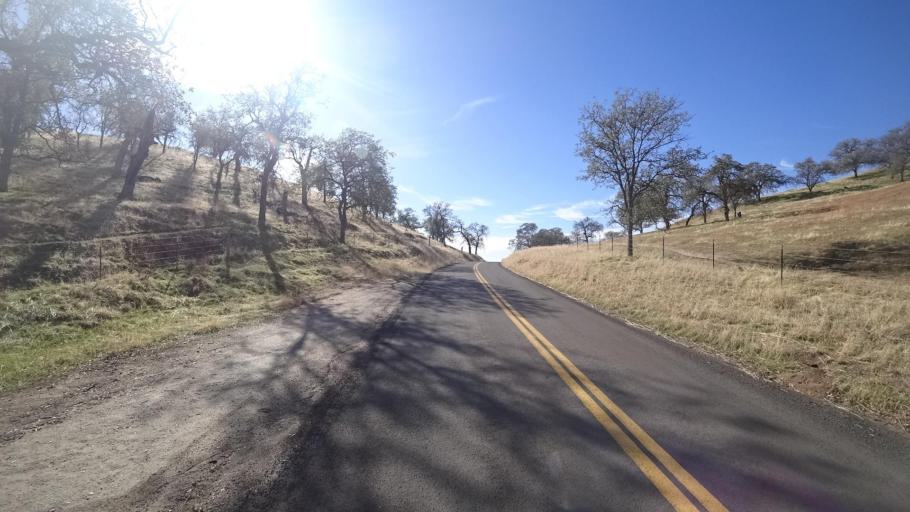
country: US
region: California
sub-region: Tulare County
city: Richgrove
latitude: 35.6859
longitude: -118.8408
